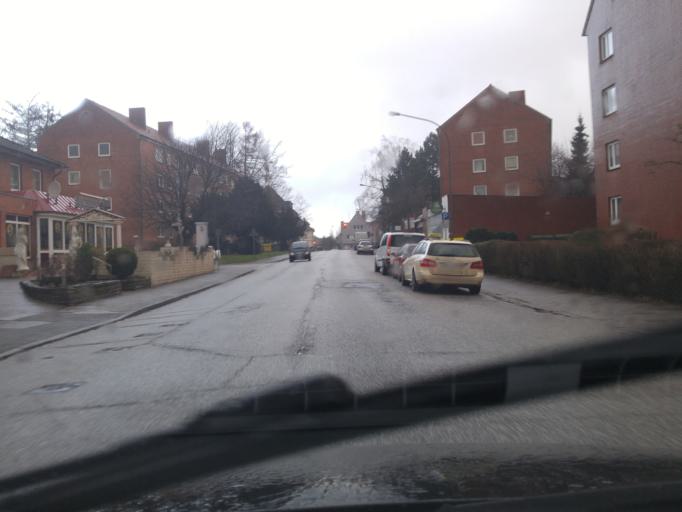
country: DE
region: Schleswig-Holstein
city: Stockelsdorf
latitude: 53.8723
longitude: 10.6606
